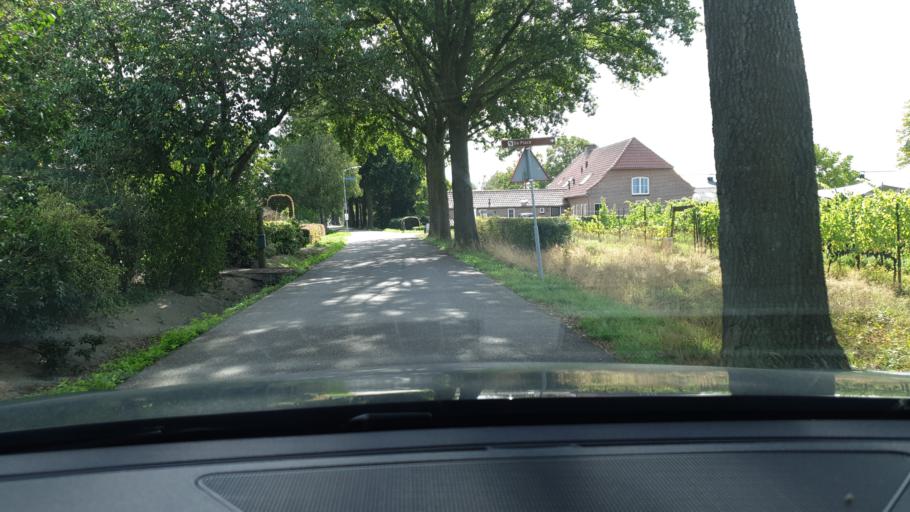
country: NL
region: Gelderland
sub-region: Gemeente Groesbeek
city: De Horst
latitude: 51.7709
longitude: 5.9844
